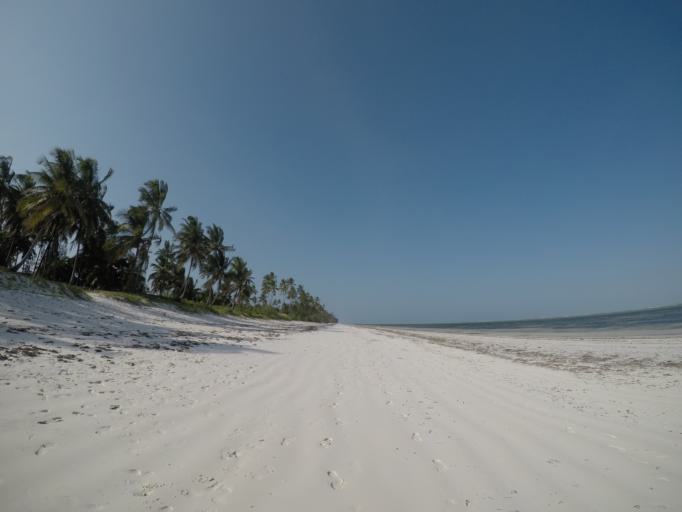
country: TZ
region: Zanzibar Central/South
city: Nganane
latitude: -6.2137
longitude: 39.5339
